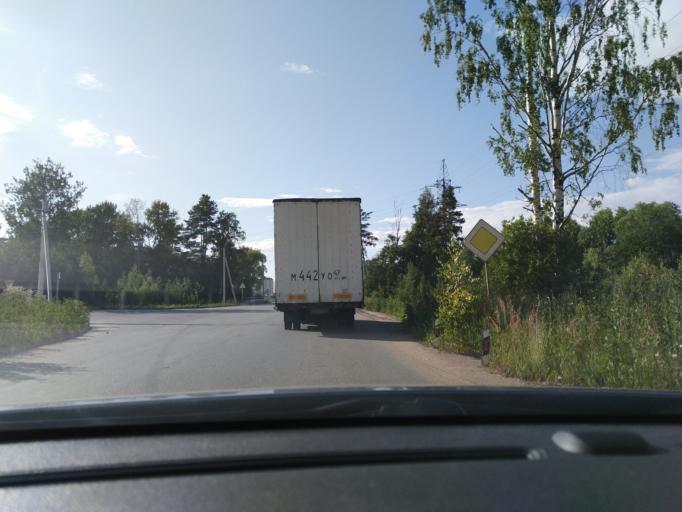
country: RU
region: St.-Petersburg
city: Gorelovo
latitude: 59.7840
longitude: 30.1695
